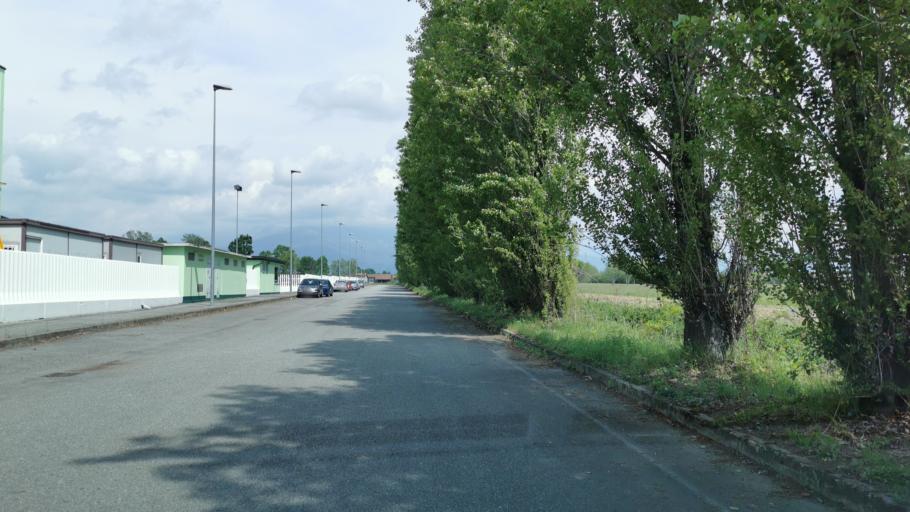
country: IT
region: Piedmont
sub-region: Provincia di Torino
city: Front
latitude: 45.3015
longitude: 7.6704
